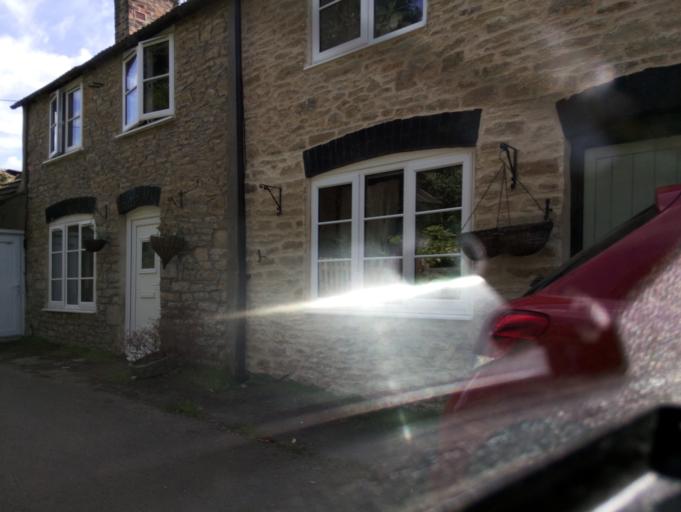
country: GB
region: England
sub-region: Gloucestershire
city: Wotton-under-Edge
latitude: 51.6447
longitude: -2.3381
